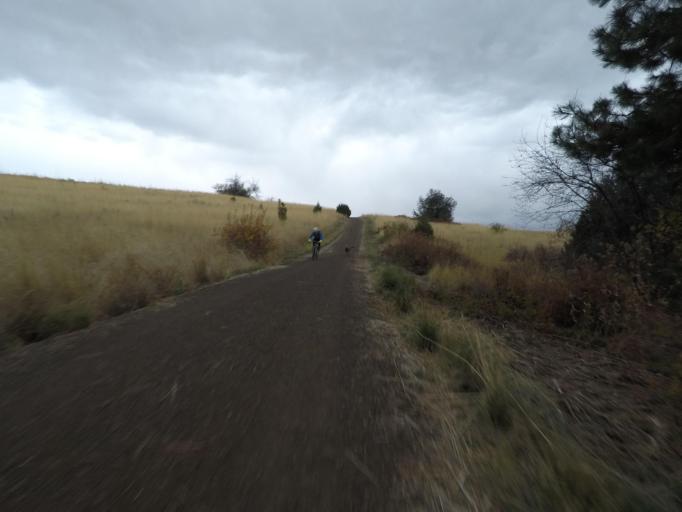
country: US
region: Washington
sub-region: Walla Walla County
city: Walla Walla East
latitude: 46.0674
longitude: -118.2564
